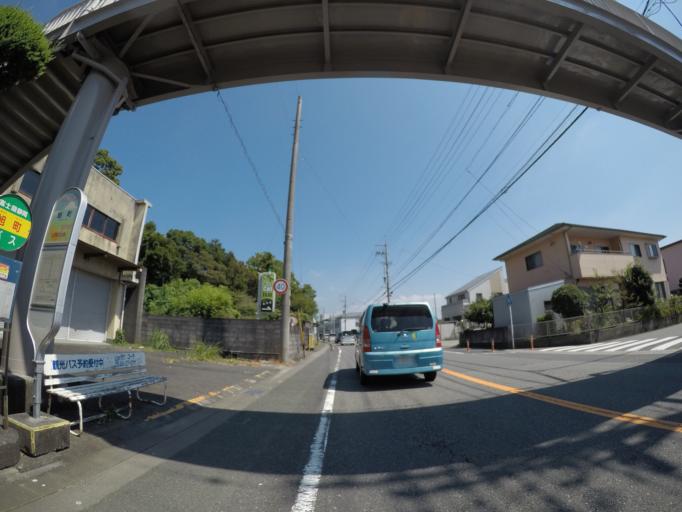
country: JP
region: Shizuoka
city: Fuji
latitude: 35.1488
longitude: 138.6208
